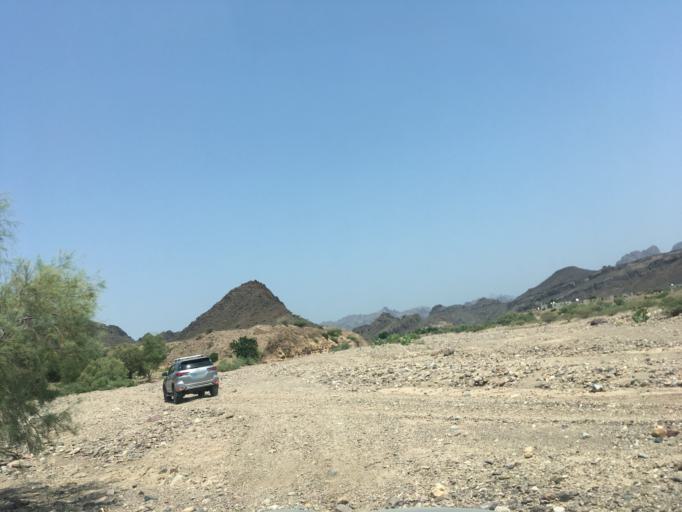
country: YE
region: Lahij
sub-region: Al Milah
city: Al Milah
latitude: 13.4404
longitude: 44.8099
